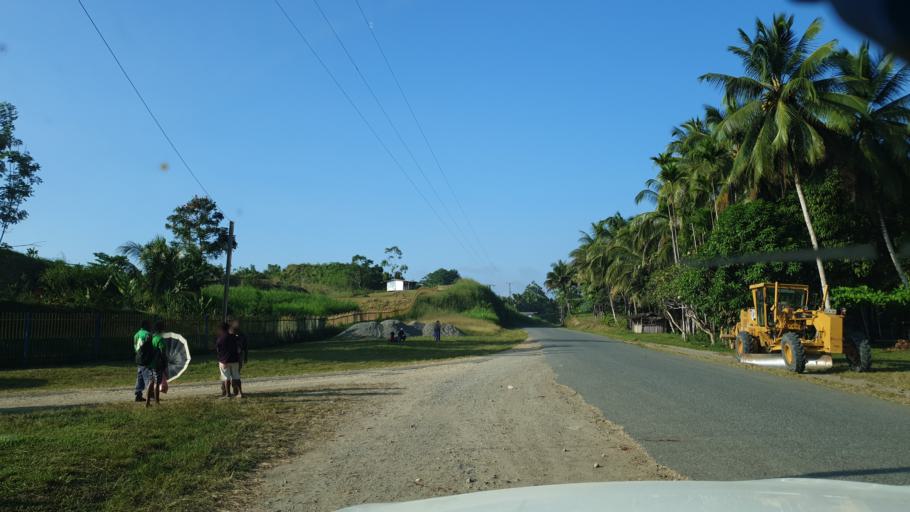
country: PG
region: East Sepik
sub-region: Wewak
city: Wewak
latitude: -3.6939
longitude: 143.6360
